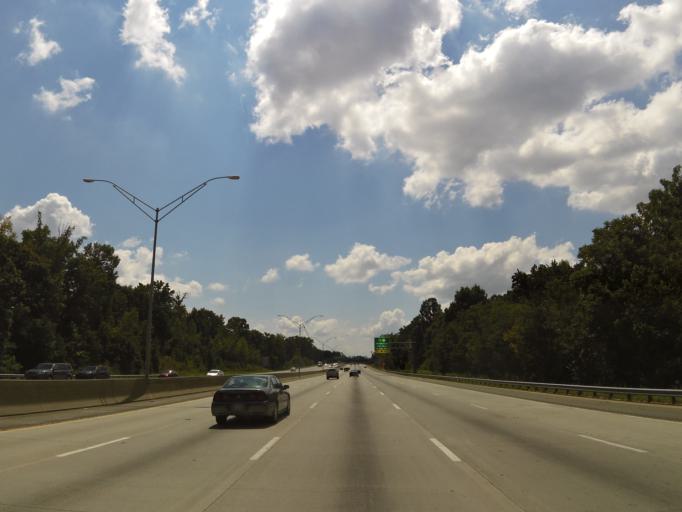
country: US
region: North Carolina
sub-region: Cabarrus County
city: Harrisburg
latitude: 35.3057
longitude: -80.7613
